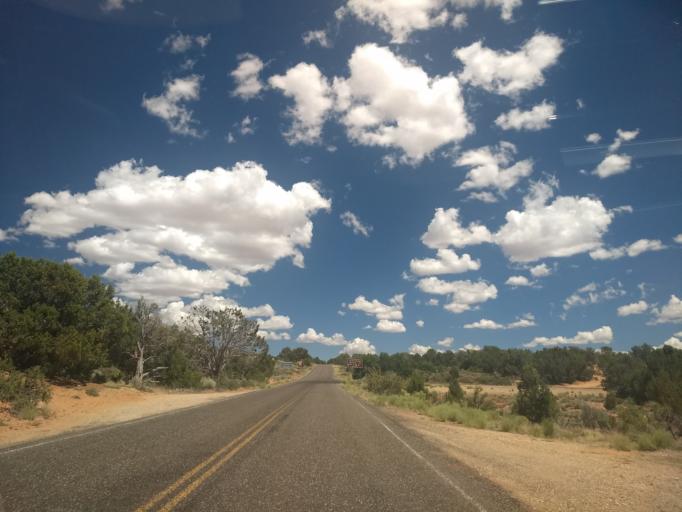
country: US
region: Utah
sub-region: Kane County
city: Kanab
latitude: 37.1867
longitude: -112.6540
